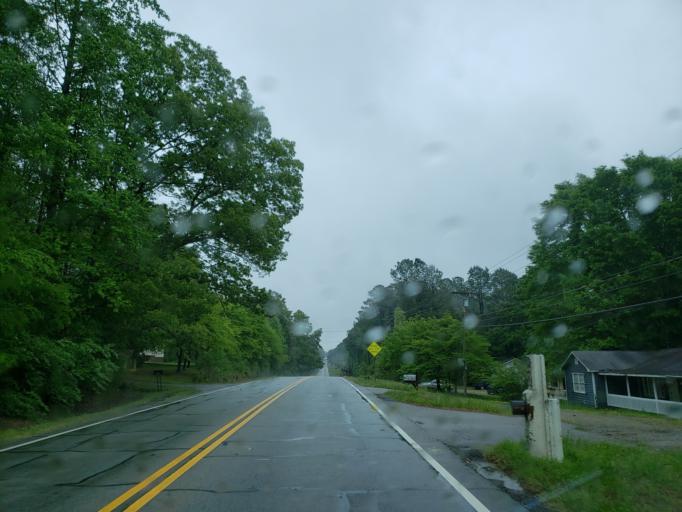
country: US
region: Georgia
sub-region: Paulding County
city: Dallas
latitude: 33.8399
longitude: -84.8646
